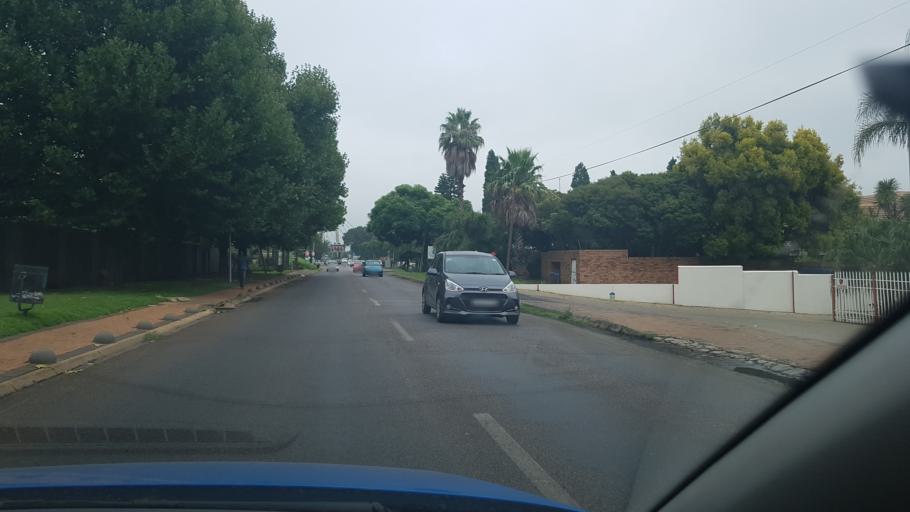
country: ZA
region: Gauteng
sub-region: Ekurhuleni Metropolitan Municipality
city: Germiston
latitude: -26.1665
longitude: 28.1496
